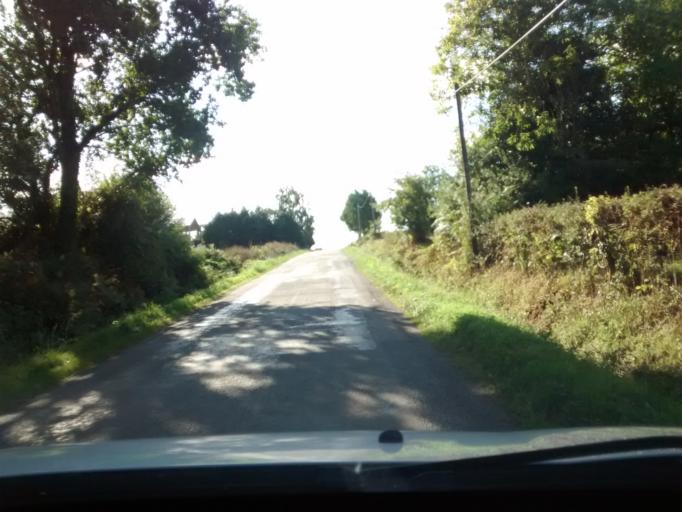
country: FR
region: Brittany
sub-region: Departement d'Ille-et-Vilaine
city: Noyal-sur-Vilaine
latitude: 48.1020
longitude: -1.5537
